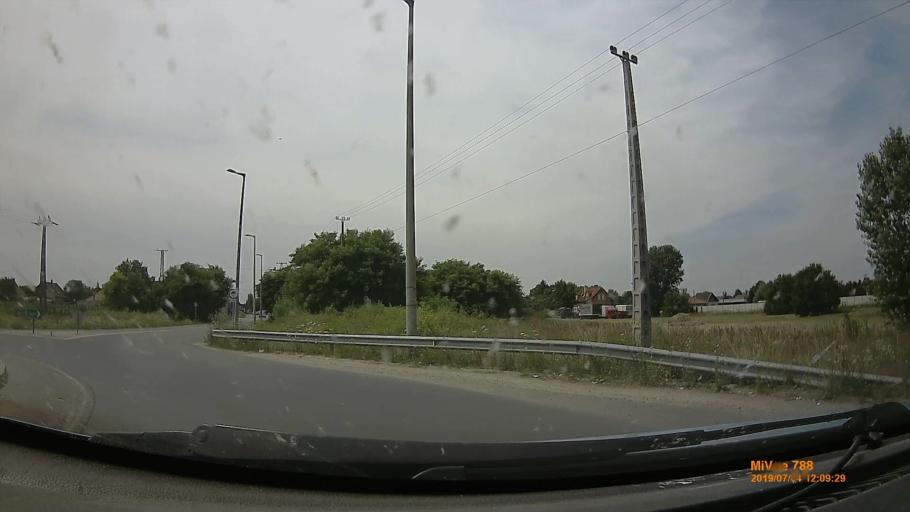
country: HU
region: Pest
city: Gyal
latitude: 47.3895
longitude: 19.2410
